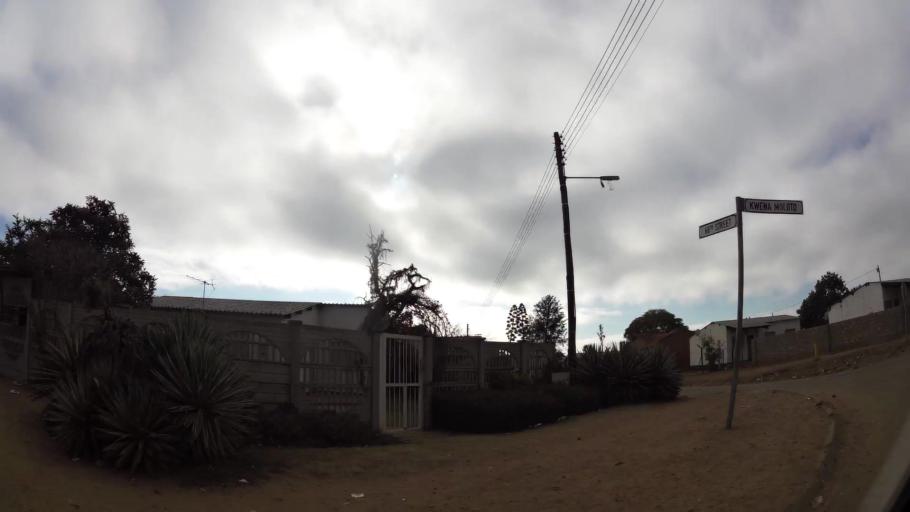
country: ZA
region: Limpopo
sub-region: Capricorn District Municipality
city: Polokwane
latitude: -23.8395
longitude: 29.3843
